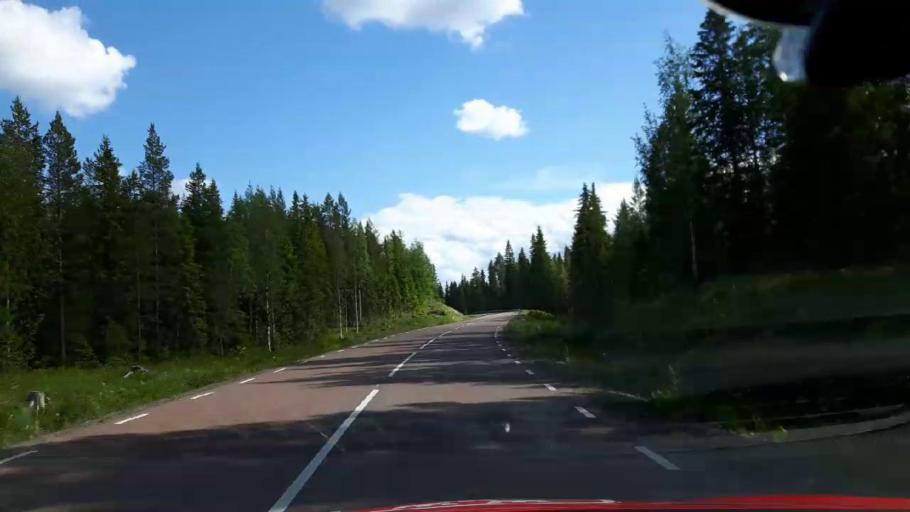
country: SE
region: Jaemtland
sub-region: Krokoms Kommun
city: Valla
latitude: 64.0624
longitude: 14.1511
